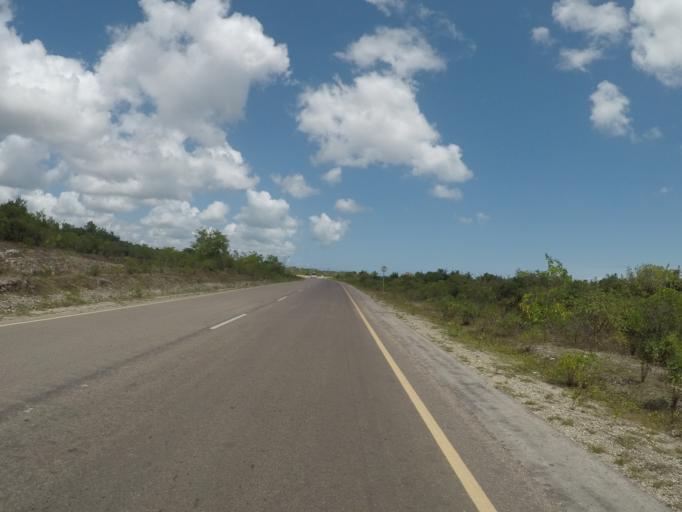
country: TZ
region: Zanzibar Central/South
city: Koani
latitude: -6.2749
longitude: 39.3645
